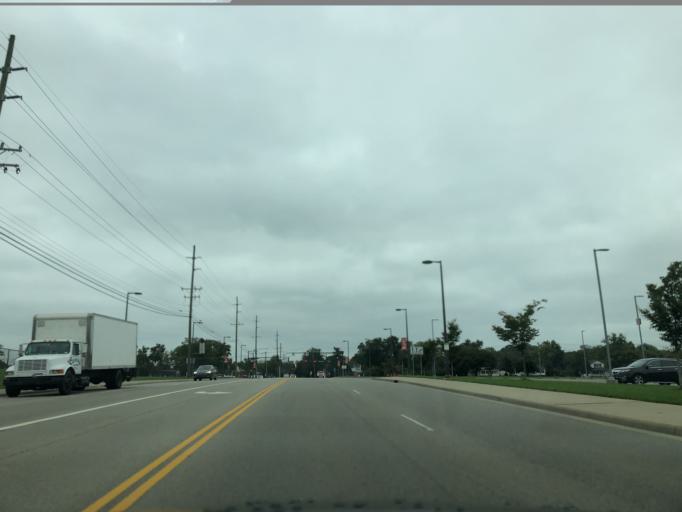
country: US
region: Ohio
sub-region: Hamilton County
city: Glendale
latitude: 39.2728
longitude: -84.4444
